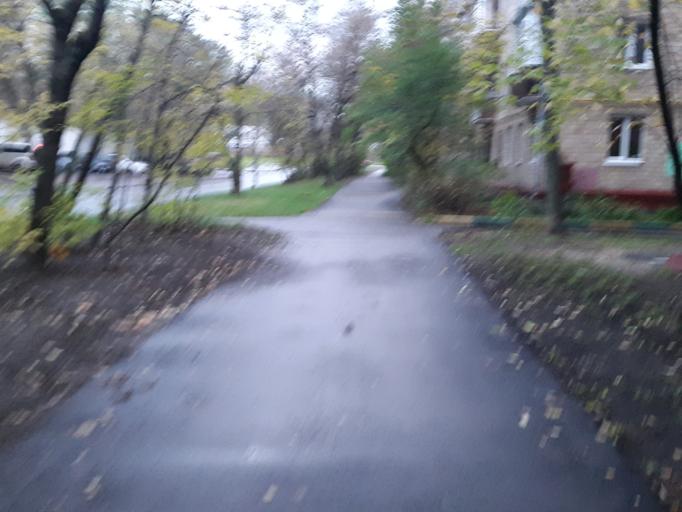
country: RU
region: Moscow
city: Pokrovskoye-Streshnevo
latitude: 55.8126
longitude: 37.4555
